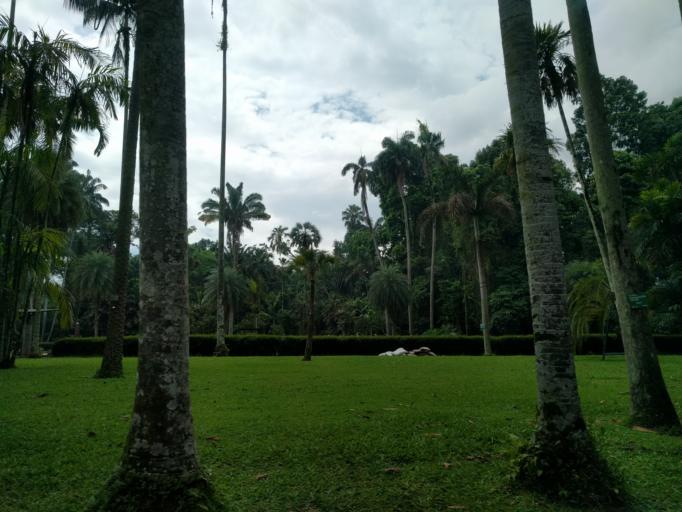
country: ID
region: West Java
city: Bogor
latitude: -6.6009
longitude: 106.7954
